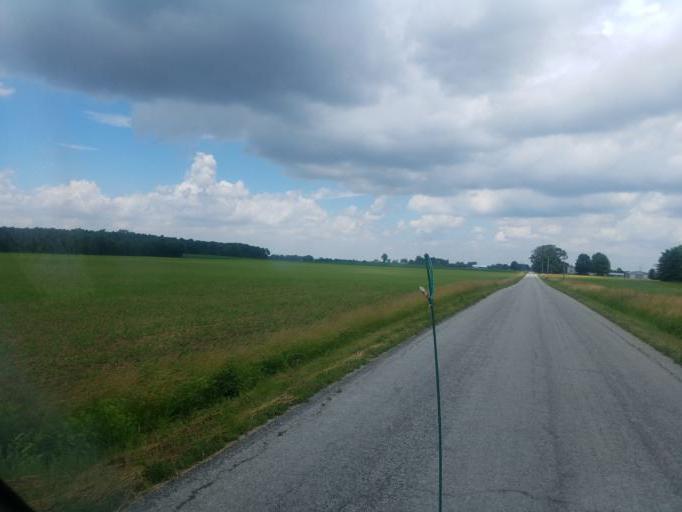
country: US
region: Ohio
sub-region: Huron County
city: Plymouth
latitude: 41.0157
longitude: -82.6318
